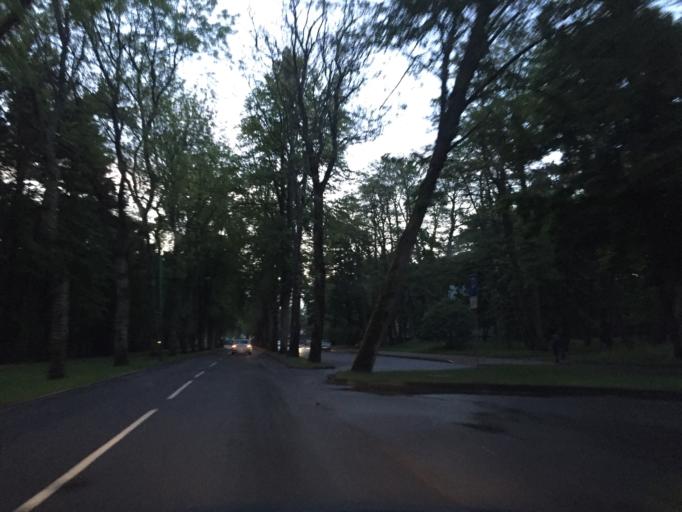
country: LT
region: Klaipedos apskritis
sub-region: Klaipeda
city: Palanga
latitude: 55.9081
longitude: 21.0621
